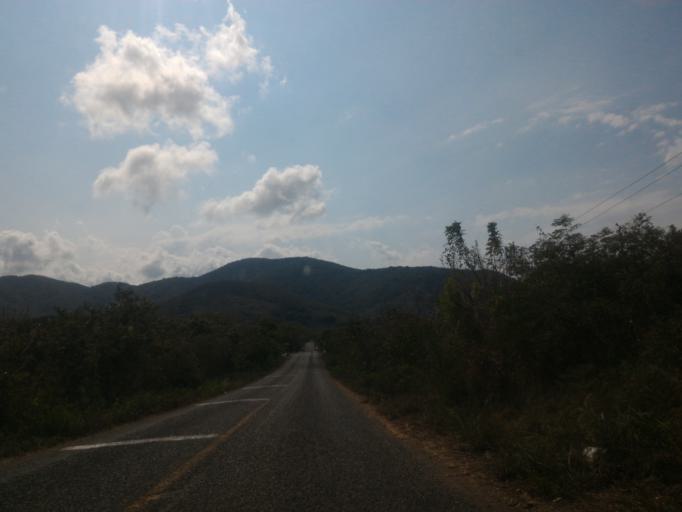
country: MX
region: Michoacan
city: Coahuayana Viejo
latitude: 18.5064
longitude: -103.5752
